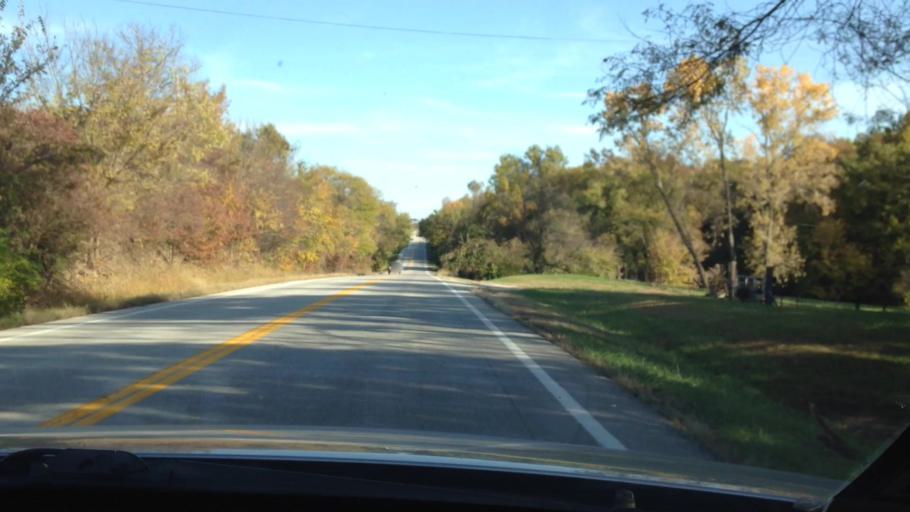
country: US
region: Missouri
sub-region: Platte County
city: Weatherby Lake
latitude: 39.2340
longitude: -94.7890
